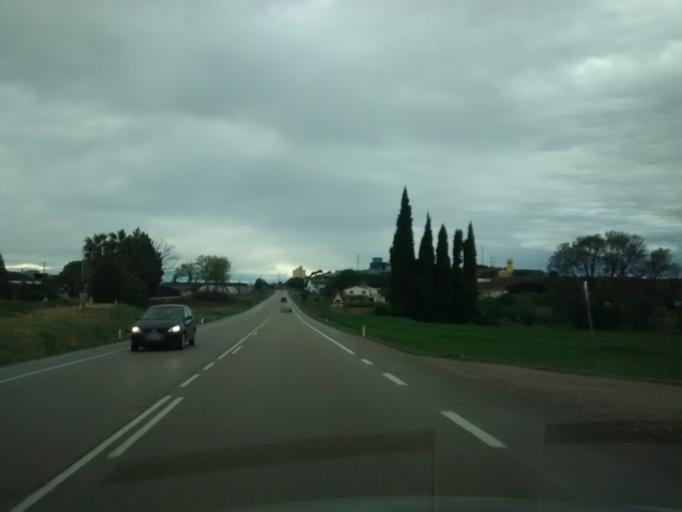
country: ES
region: Aragon
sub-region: Provincia de Zaragoza
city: Caspe
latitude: 41.2225
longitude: -0.0214
